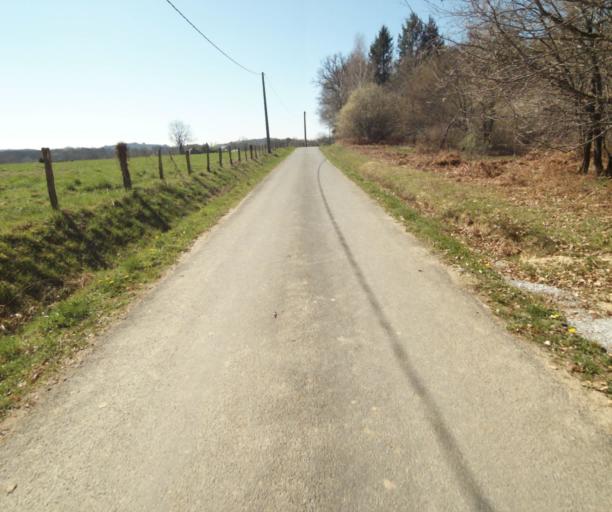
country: FR
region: Limousin
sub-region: Departement de la Correze
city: Saint-Mexant
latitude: 45.3103
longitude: 1.6555
